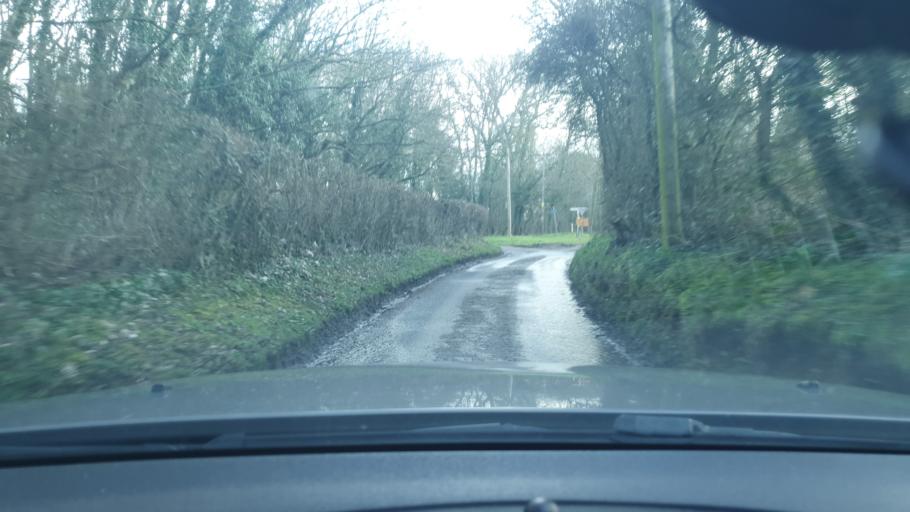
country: GB
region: England
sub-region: Wokingham
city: Wargrave
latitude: 51.5238
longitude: -0.8418
